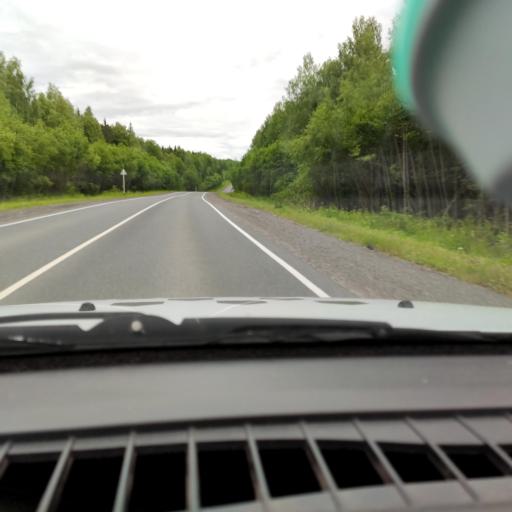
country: RU
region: Perm
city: Chusovoy
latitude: 58.2186
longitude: 57.8234
